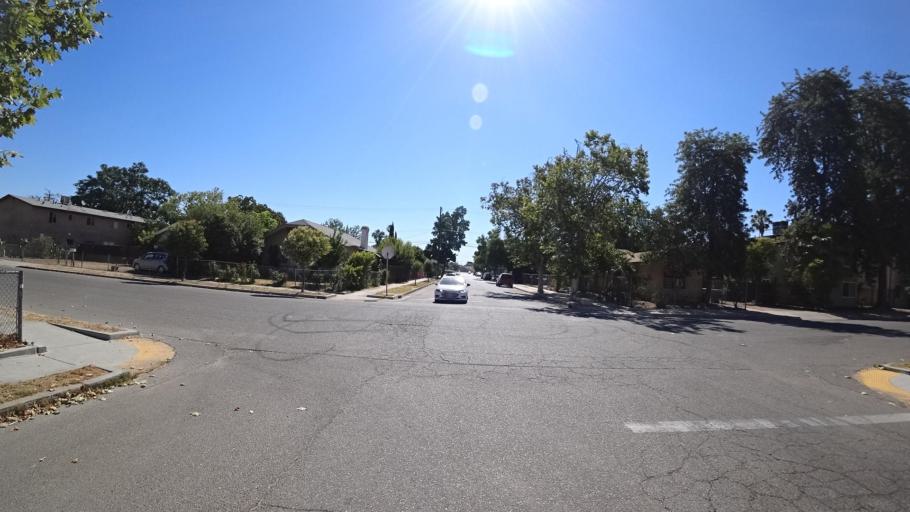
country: US
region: California
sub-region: Fresno County
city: Fresno
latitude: 36.7488
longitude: -119.8058
